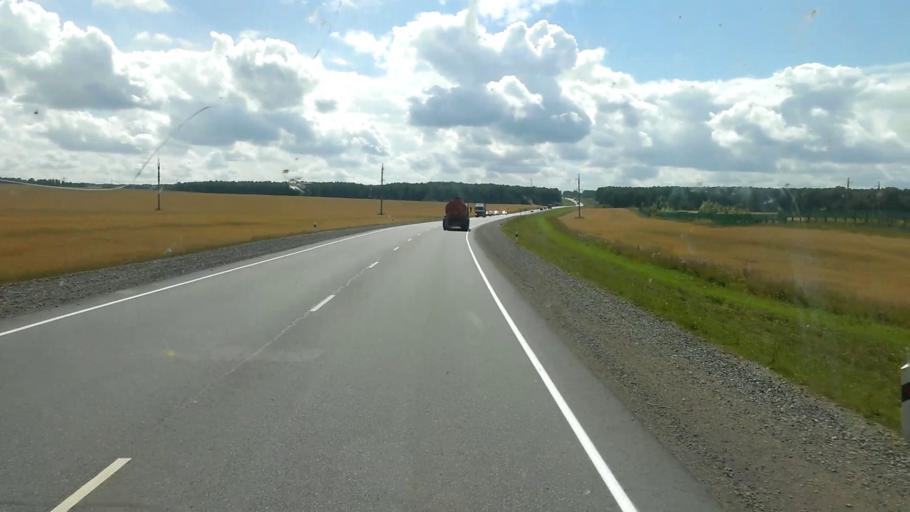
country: RU
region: Altai Krai
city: Troitskoye
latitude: 52.9920
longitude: 84.7418
